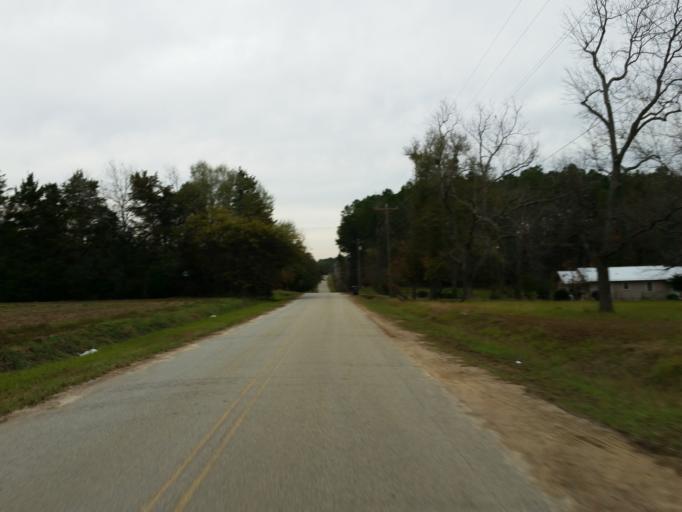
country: US
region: Georgia
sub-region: Crisp County
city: Cordele
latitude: 31.9197
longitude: -83.7283
